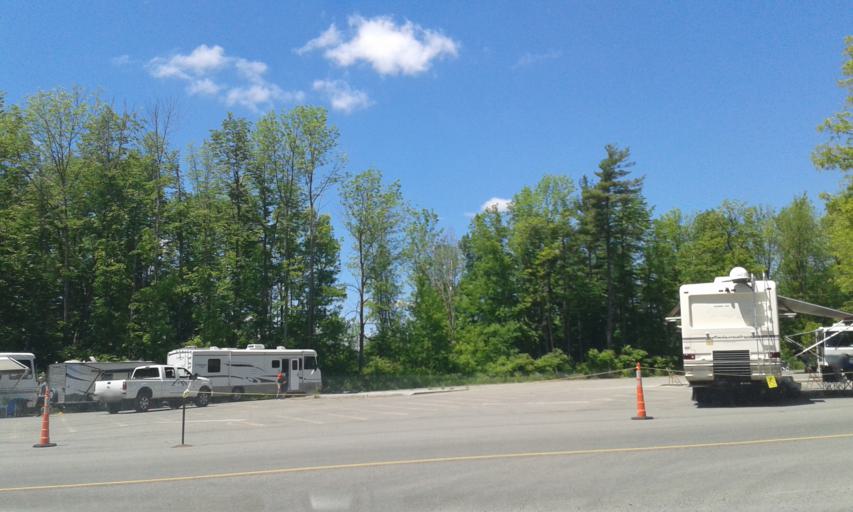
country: US
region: New York
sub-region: St. Lawrence County
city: Massena
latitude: 45.0166
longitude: -74.8941
